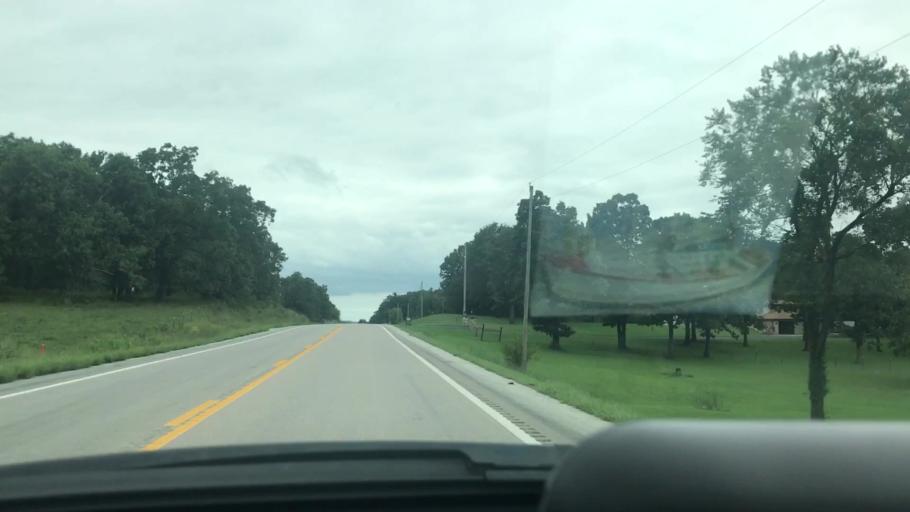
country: US
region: Missouri
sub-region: Dallas County
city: Buffalo
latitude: 37.7098
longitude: -93.1140
